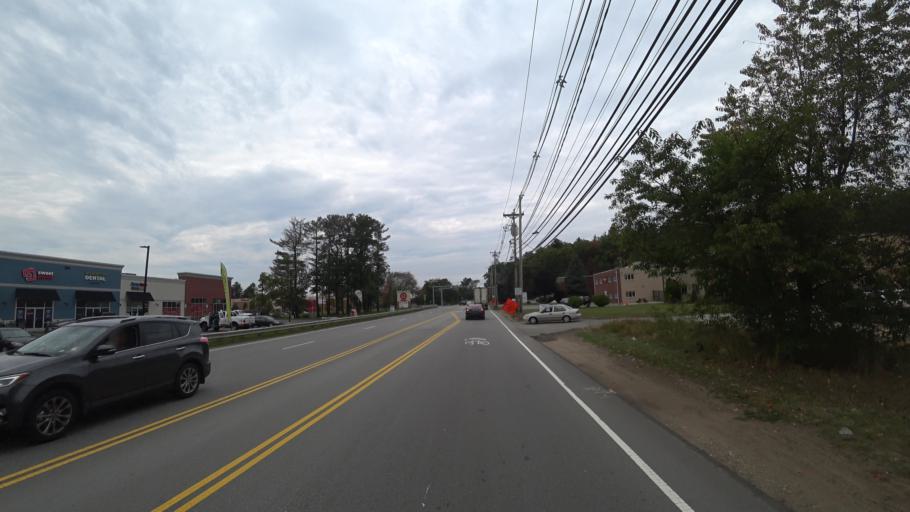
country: US
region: Massachusetts
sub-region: Middlesex County
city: Wilmington
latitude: 42.5892
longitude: -71.1577
